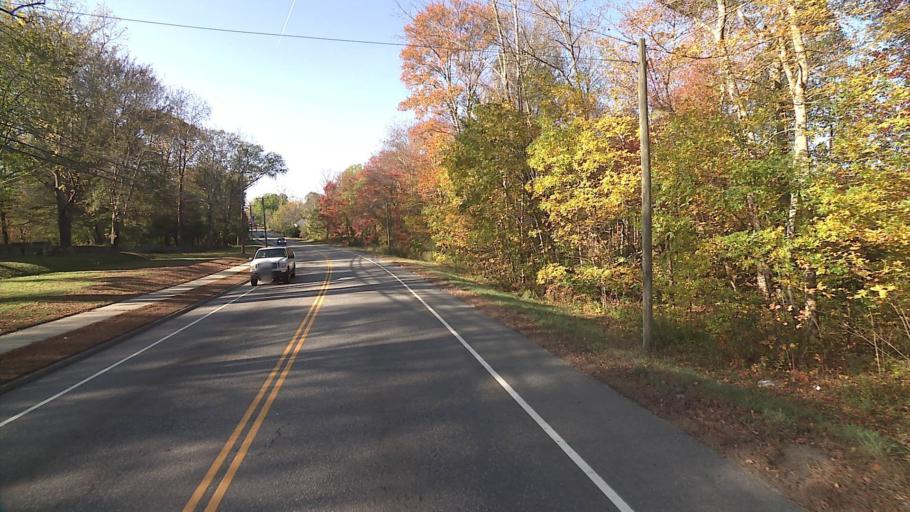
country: US
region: Connecticut
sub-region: Windham County
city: East Brooklyn
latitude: 41.7922
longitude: -71.9461
